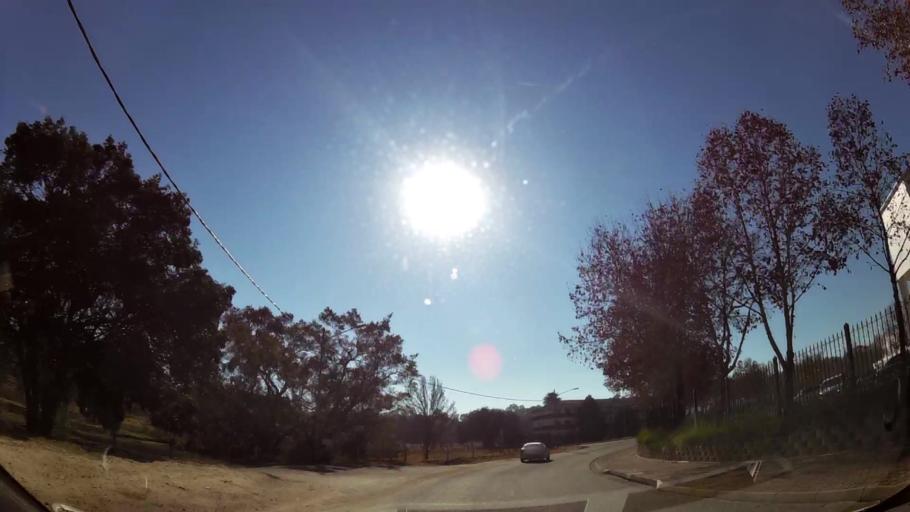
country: ZA
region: Gauteng
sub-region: City of Tshwane Metropolitan Municipality
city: Centurion
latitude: -25.8555
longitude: 28.2155
